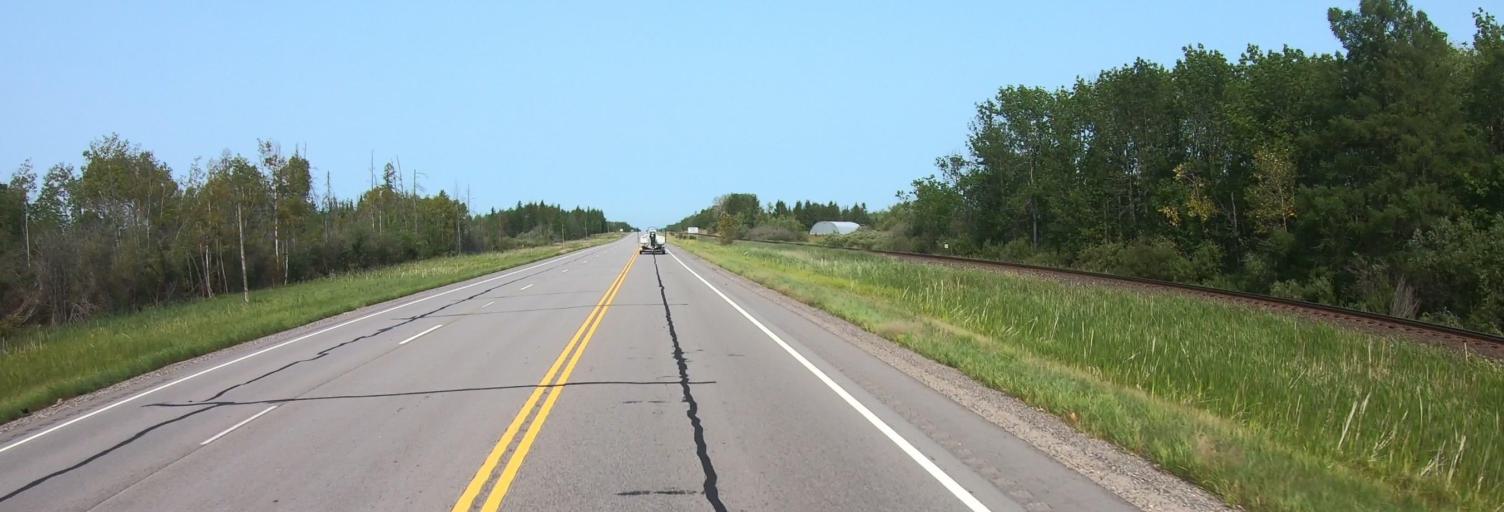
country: CA
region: Ontario
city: Fort Frances
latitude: 48.4422
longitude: -93.2581
